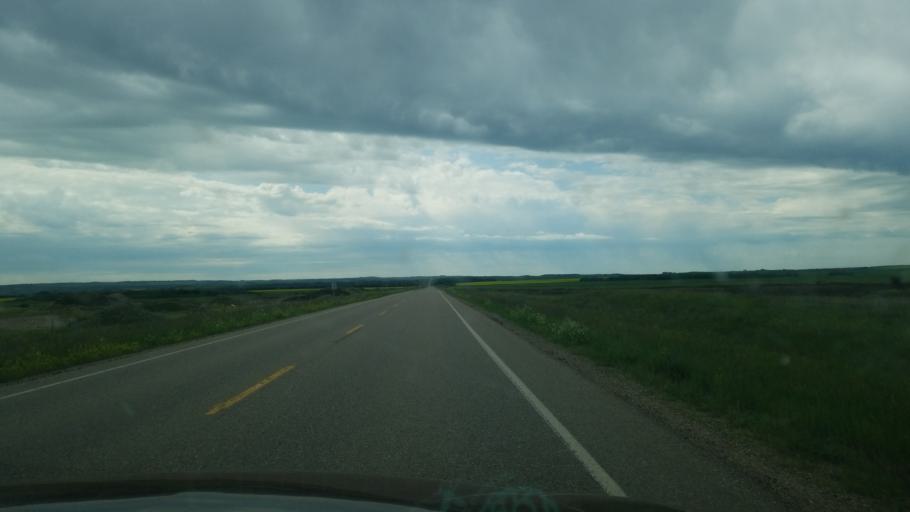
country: CA
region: Saskatchewan
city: Unity
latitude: 52.9647
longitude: -109.3426
